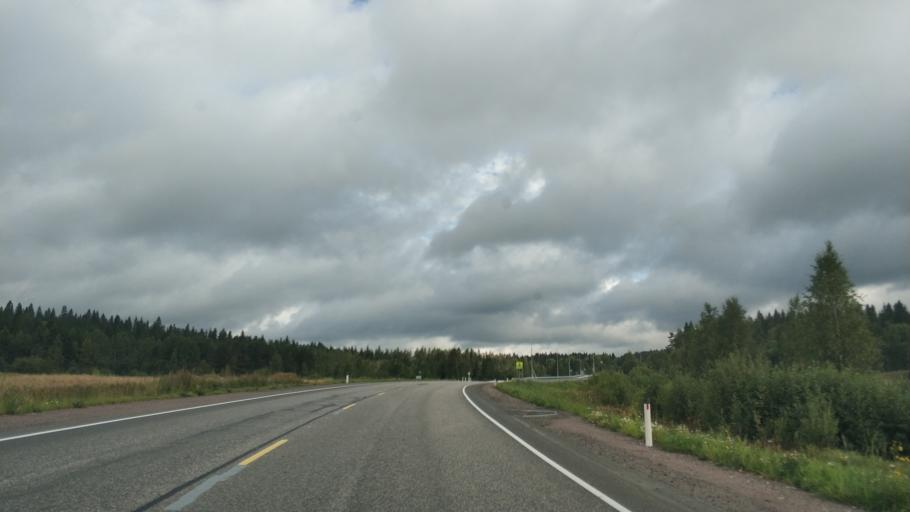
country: RU
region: Republic of Karelia
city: Khelyulya
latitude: 61.7989
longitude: 30.6154
